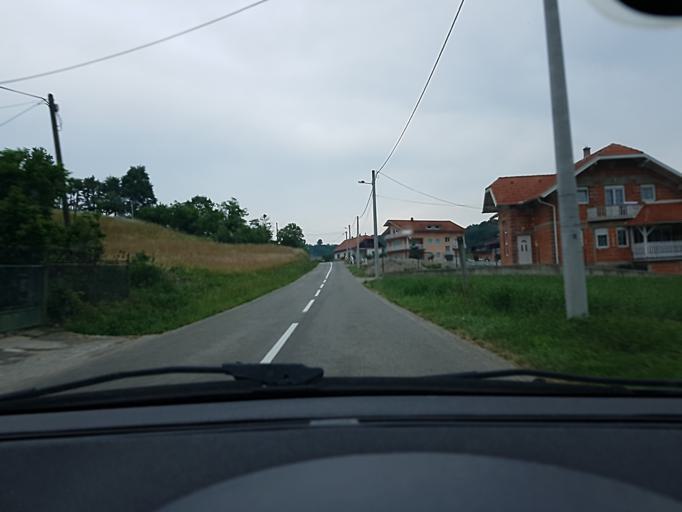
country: HR
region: Zagrebacka
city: Jakovlje
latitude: 45.9639
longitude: 15.8257
